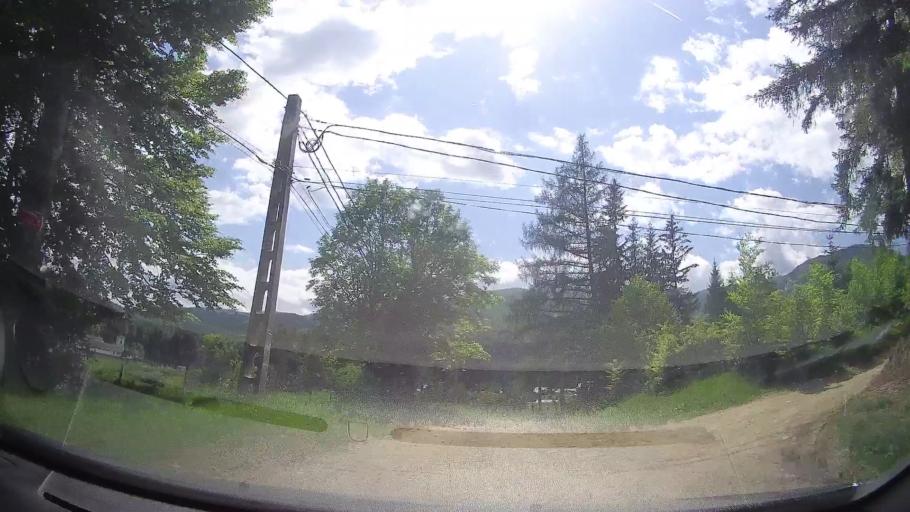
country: RO
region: Brasov
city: Crivina
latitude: 45.4584
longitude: 25.9437
